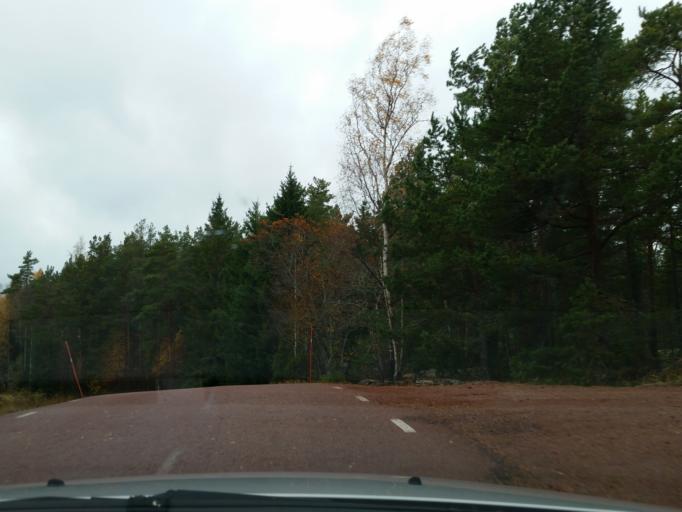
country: AX
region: Alands landsbygd
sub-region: Lumparland
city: Lumparland
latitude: 60.1509
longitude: 20.2861
